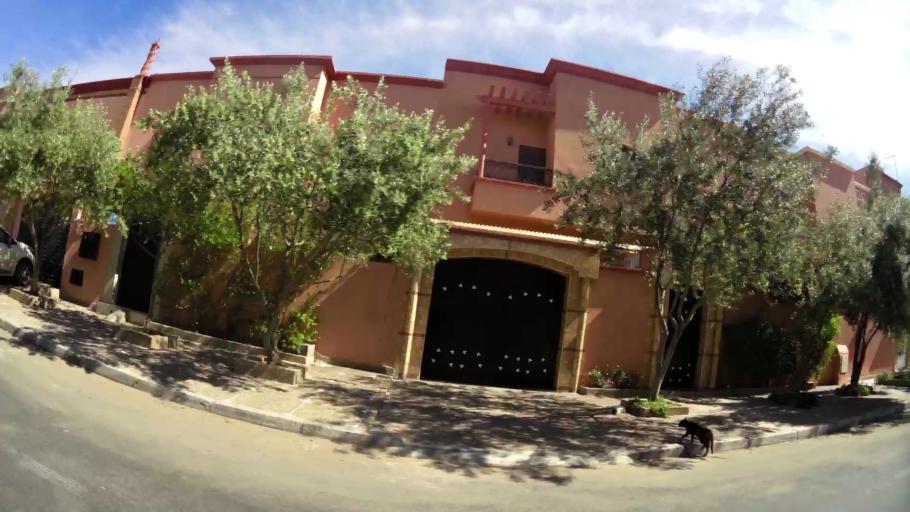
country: MA
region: Marrakech-Tensift-Al Haouz
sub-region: Marrakech
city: Marrakesh
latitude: 31.6360
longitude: -8.0409
